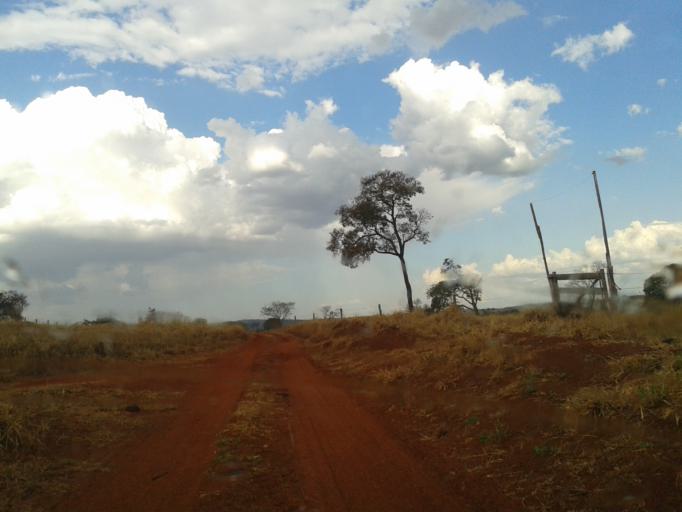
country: BR
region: Minas Gerais
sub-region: Santa Vitoria
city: Santa Vitoria
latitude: -19.1707
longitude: -49.9697
